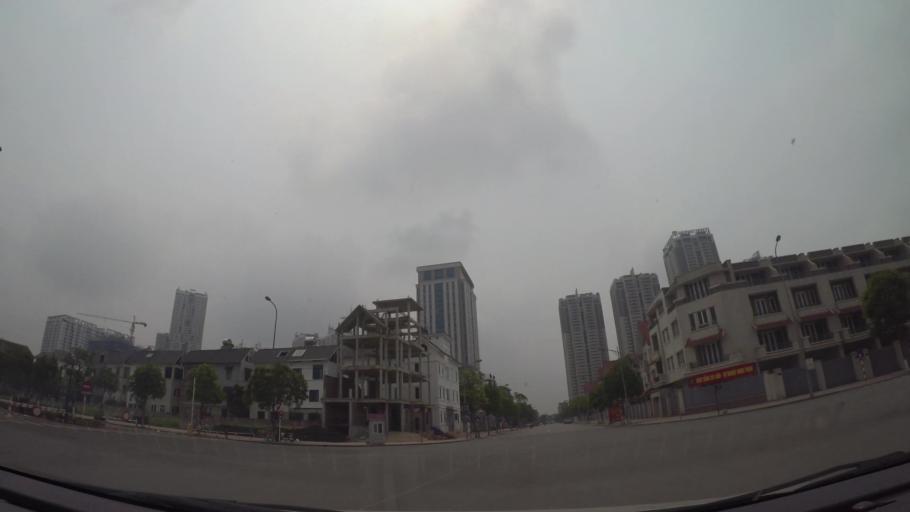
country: VN
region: Ha Noi
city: Ha Dong
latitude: 20.9759
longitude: 105.7562
